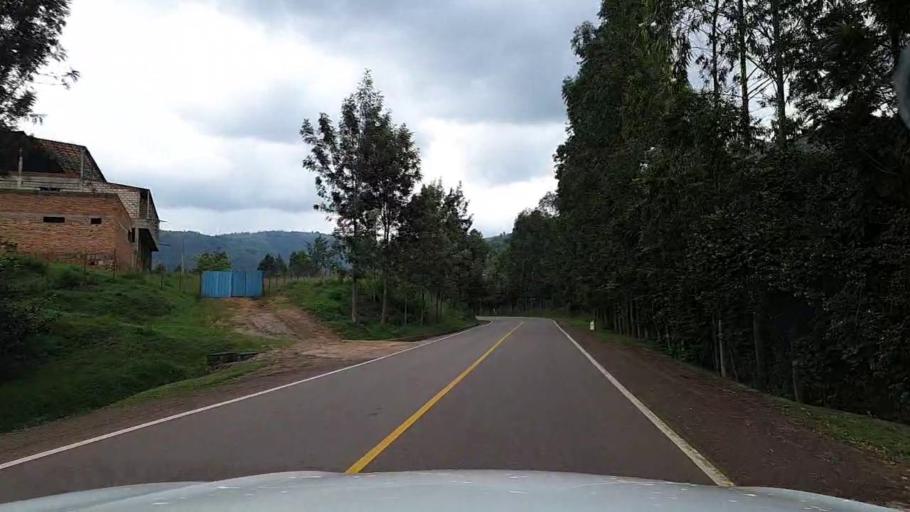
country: RW
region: Northern Province
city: Byumba
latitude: -1.6831
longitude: 30.1042
